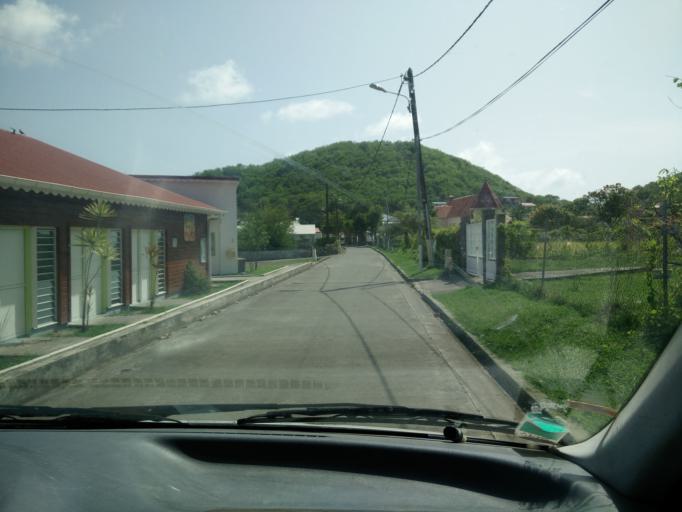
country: GP
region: Guadeloupe
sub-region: Guadeloupe
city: Terre-de-Bas
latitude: 15.8509
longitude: -61.6431
